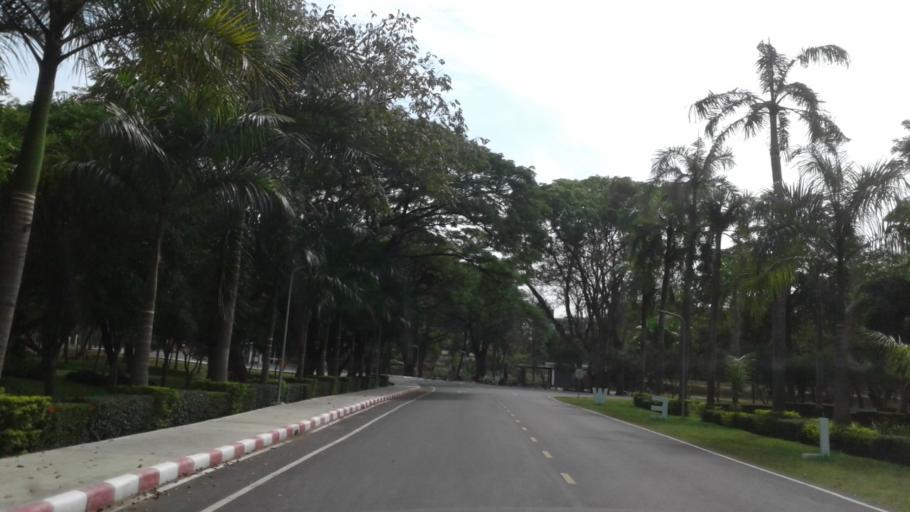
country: TH
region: Pathum Thani
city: Khlong Luang
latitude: 14.0776
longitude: 100.6139
